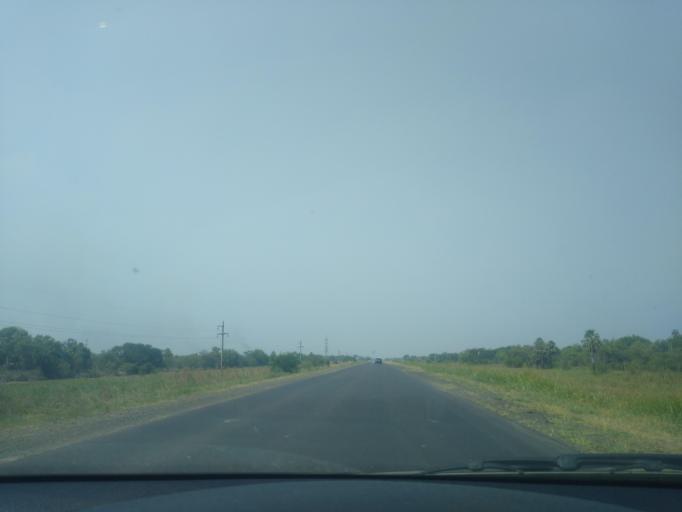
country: AR
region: Chaco
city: Fontana
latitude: -27.4998
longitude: -59.0836
